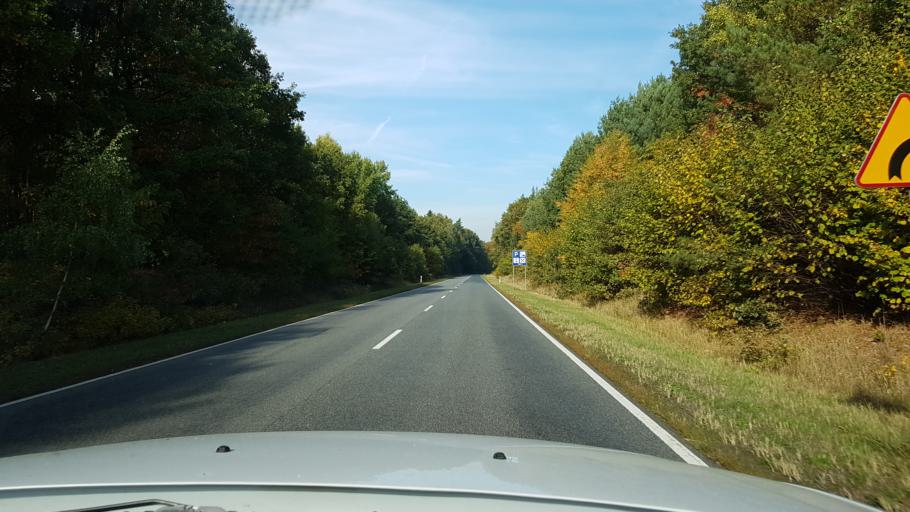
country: PL
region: West Pomeranian Voivodeship
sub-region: Powiat mysliborski
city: Nowogrodek Pomorski
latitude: 52.9270
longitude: 14.9573
